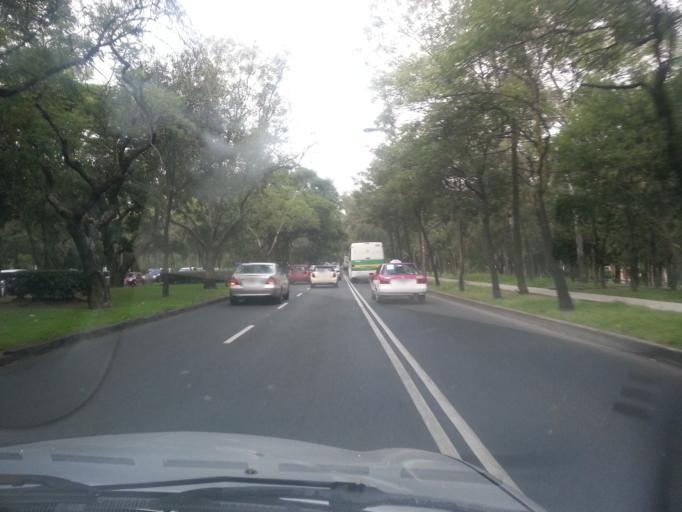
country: MX
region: Mexico City
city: Polanco
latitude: 19.4111
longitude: -99.2216
